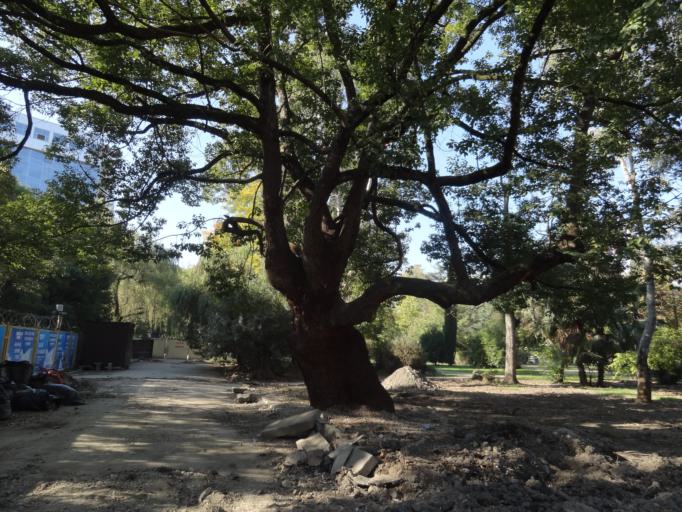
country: RU
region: Krasnodarskiy
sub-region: Sochi City
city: Sochi
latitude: 43.5850
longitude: 39.7221
